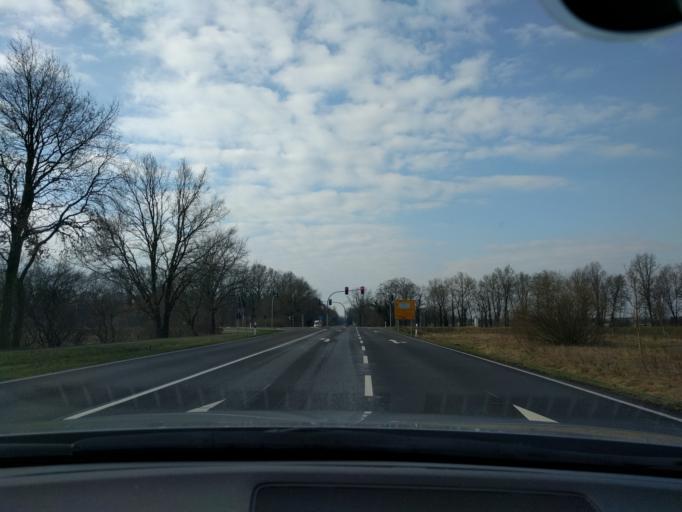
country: DE
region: Saxony-Anhalt
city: Stendal
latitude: 52.6306
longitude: 11.8801
